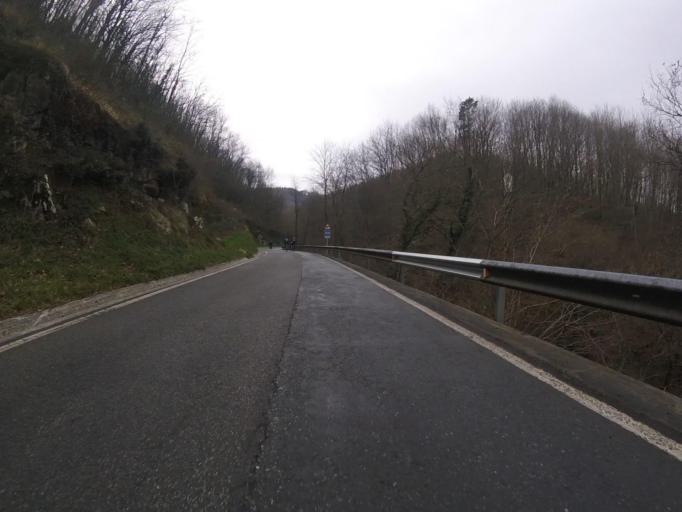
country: ES
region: Navarre
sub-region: Provincia de Navarra
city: Arantza
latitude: 43.2029
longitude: -1.7151
